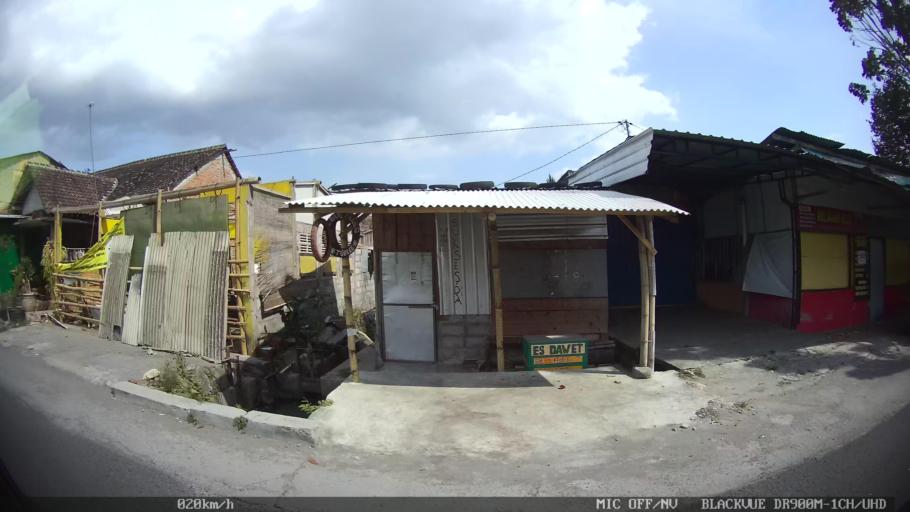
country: ID
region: Daerah Istimewa Yogyakarta
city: Kasihan
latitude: -7.8154
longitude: 110.3292
